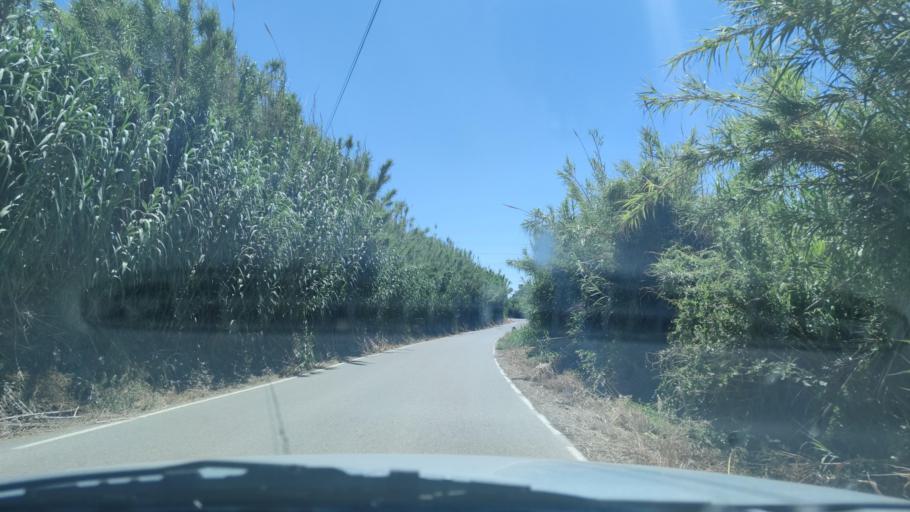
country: ES
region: Catalonia
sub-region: Provincia de Lleida
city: Alcoletge
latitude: 41.6398
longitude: 0.6613
